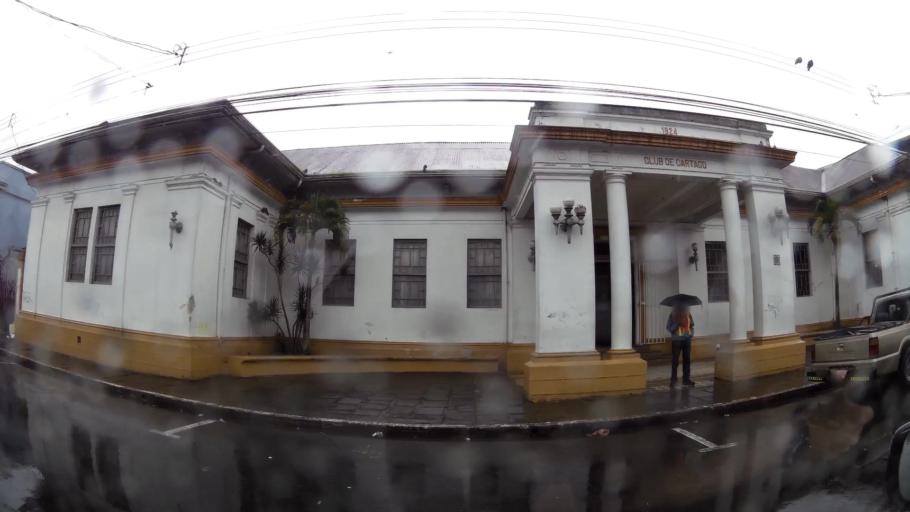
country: CR
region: Cartago
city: Cartago
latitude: 9.8649
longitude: -83.9216
